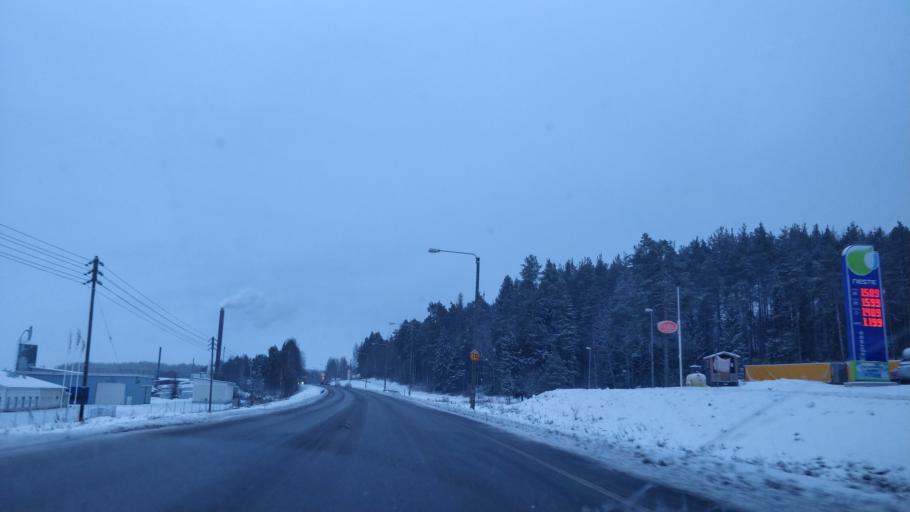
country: FI
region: Central Finland
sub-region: Saarijaervi-Viitasaari
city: Viitasaari
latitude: 63.0846
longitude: 25.8629
